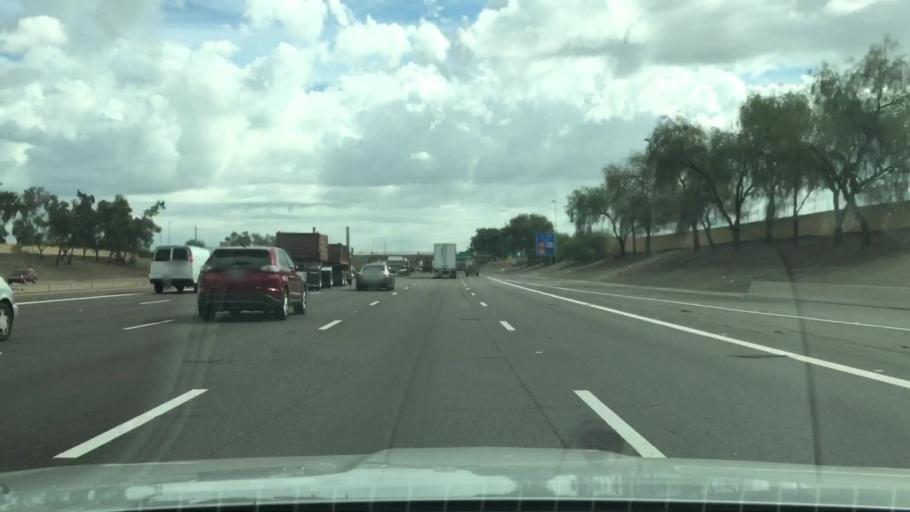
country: US
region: Arizona
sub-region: Maricopa County
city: Tolleson
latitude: 33.4616
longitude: -112.2342
